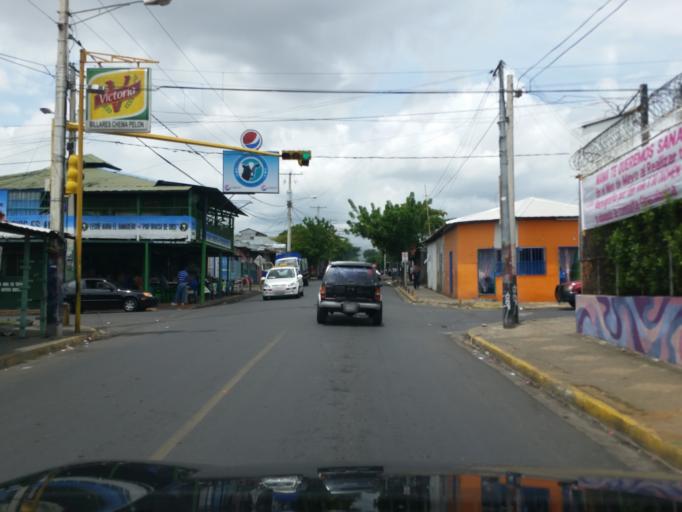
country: NI
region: Managua
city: Managua
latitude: 12.1387
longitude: -86.2534
